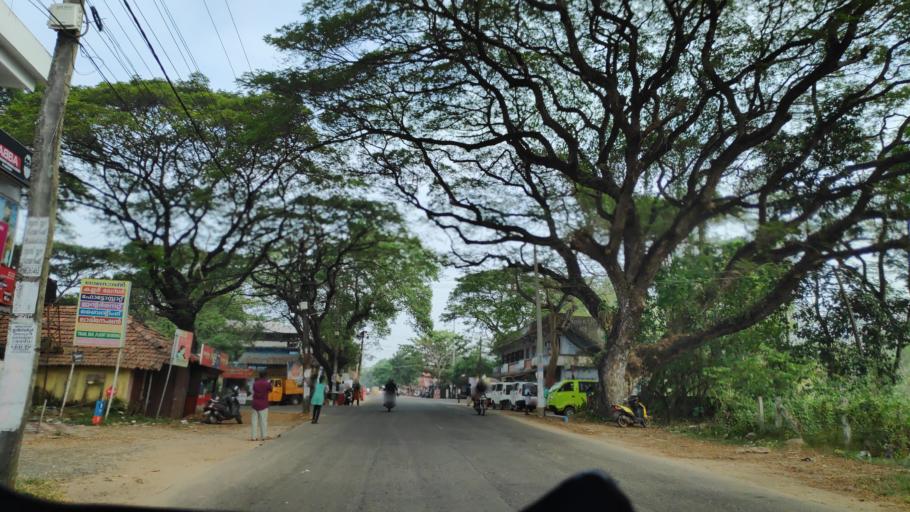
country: IN
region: Kerala
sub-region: Kottayam
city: Vaikam
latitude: 9.7512
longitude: 76.3632
